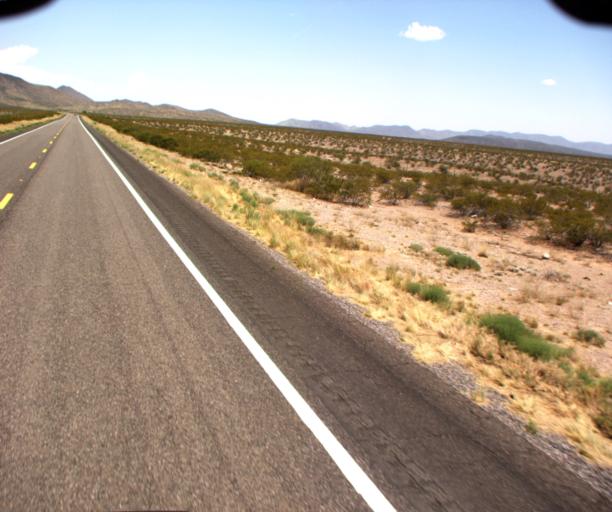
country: US
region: Arizona
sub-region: Greenlee County
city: Clifton
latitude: 32.7527
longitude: -109.3536
